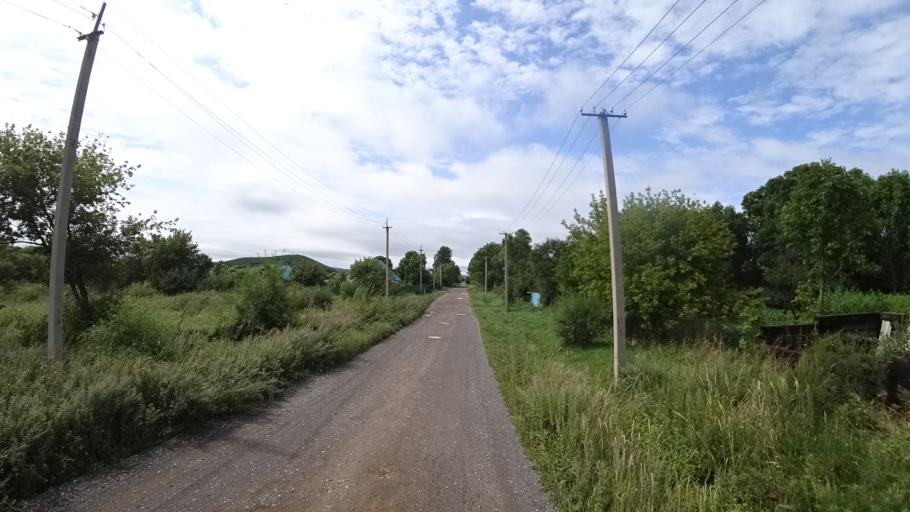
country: RU
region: Primorskiy
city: Lyalichi
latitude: 44.1385
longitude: 132.3851
